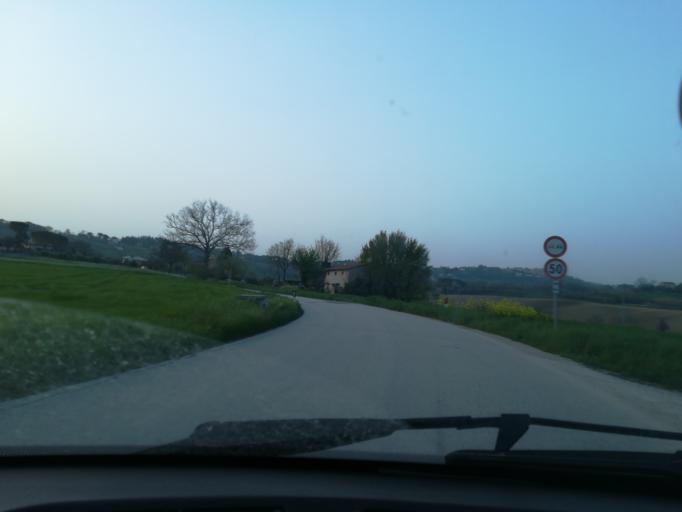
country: IT
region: The Marches
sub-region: Provincia di Macerata
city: Macerata
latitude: 43.2733
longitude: 13.4570
